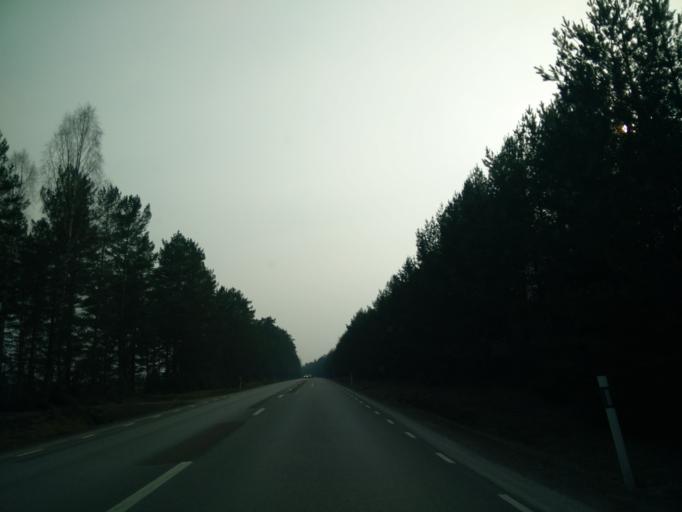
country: SE
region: Vaermland
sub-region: Forshaga Kommun
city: Forshaga
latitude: 59.4885
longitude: 13.4205
